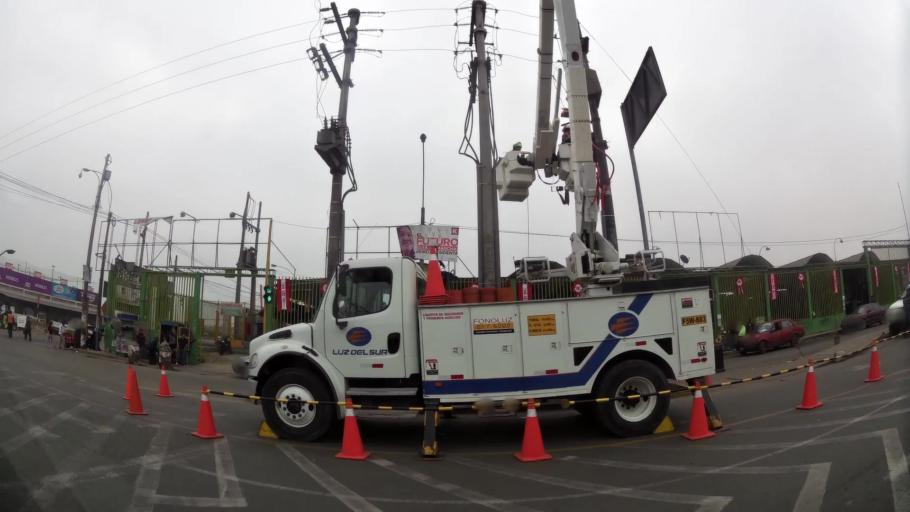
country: PE
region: Lima
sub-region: Lima
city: Vitarte
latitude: -12.0437
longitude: -76.9378
